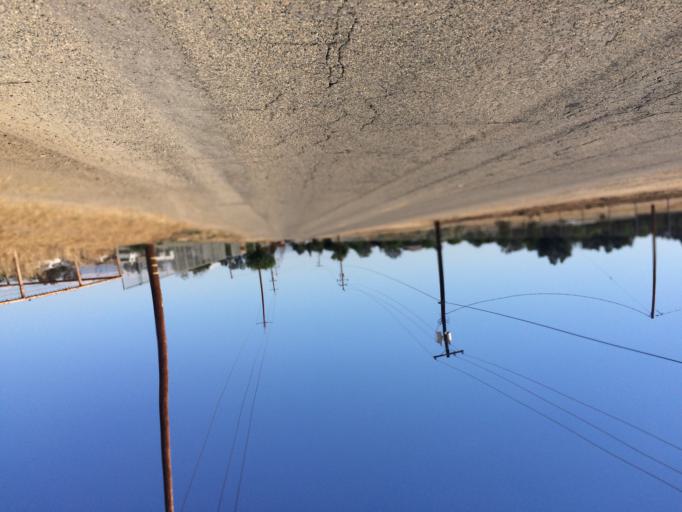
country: US
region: California
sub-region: Fresno County
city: Sanger
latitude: 36.7623
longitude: -119.6101
